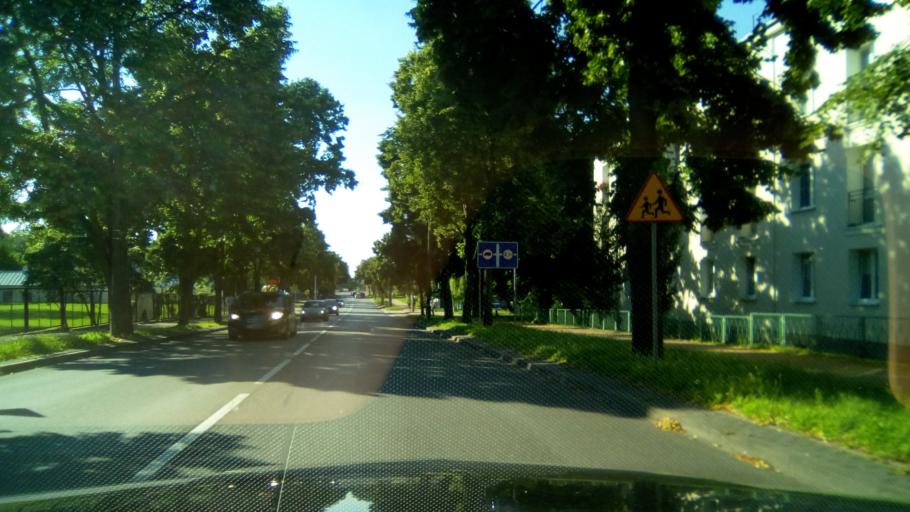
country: PL
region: Lublin Voivodeship
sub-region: Powiat pulawski
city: Pulawy
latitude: 51.4148
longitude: 21.9602
